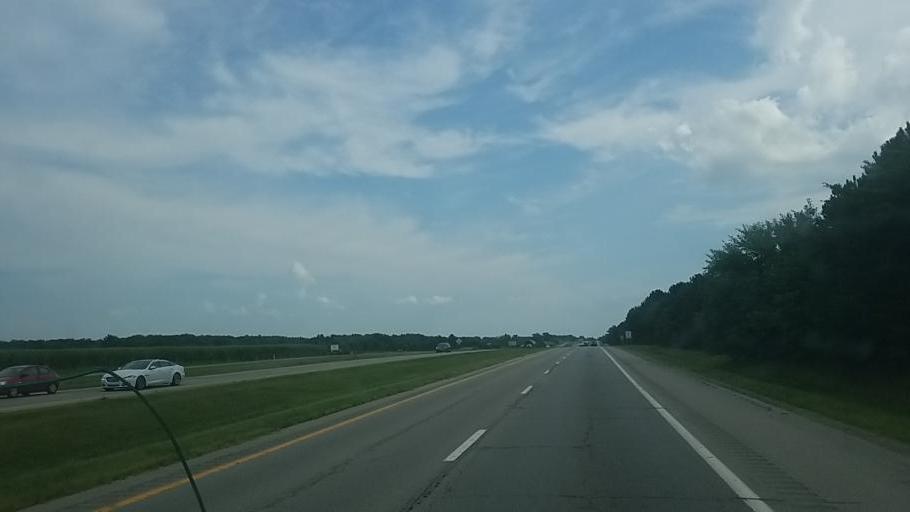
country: US
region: Ohio
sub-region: Wyandot County
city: Upper Sandusky
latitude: 40.7736
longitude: -83.2414
